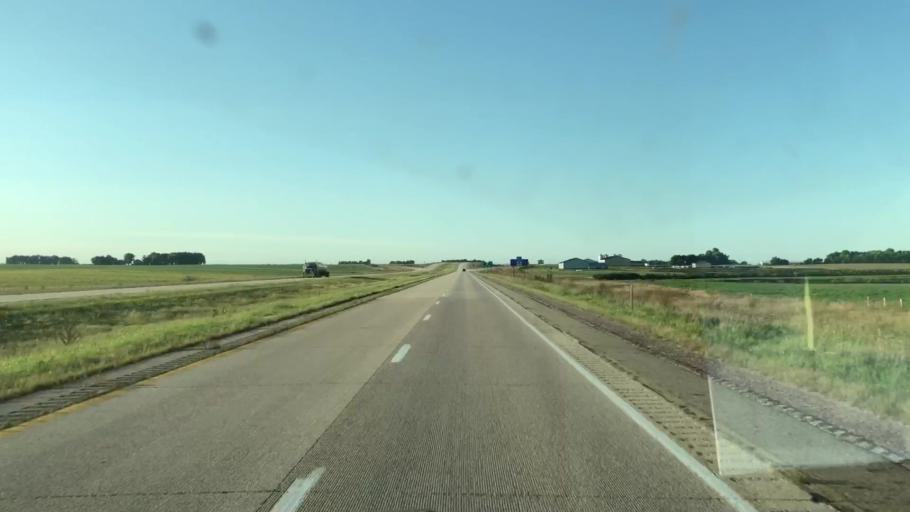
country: US
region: Iowa
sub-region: Osceola County
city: Sibley
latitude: 43.4435
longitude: -95.7137
